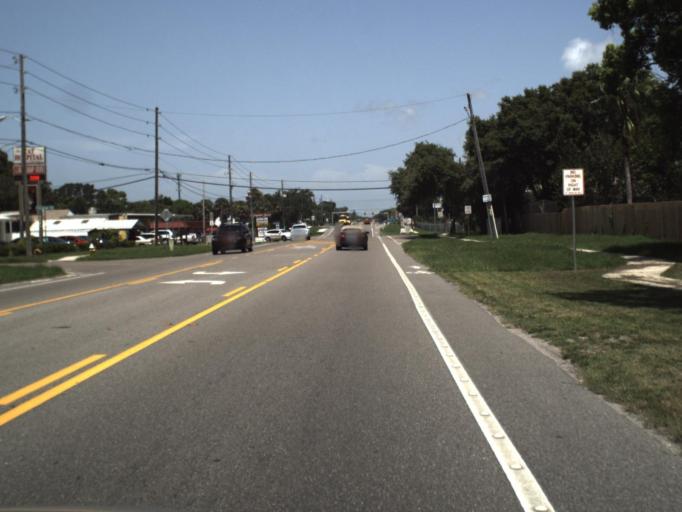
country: US
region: Florida
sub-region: Pinellas County
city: Palm Harbor
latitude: 28.0897
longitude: -82.7724
